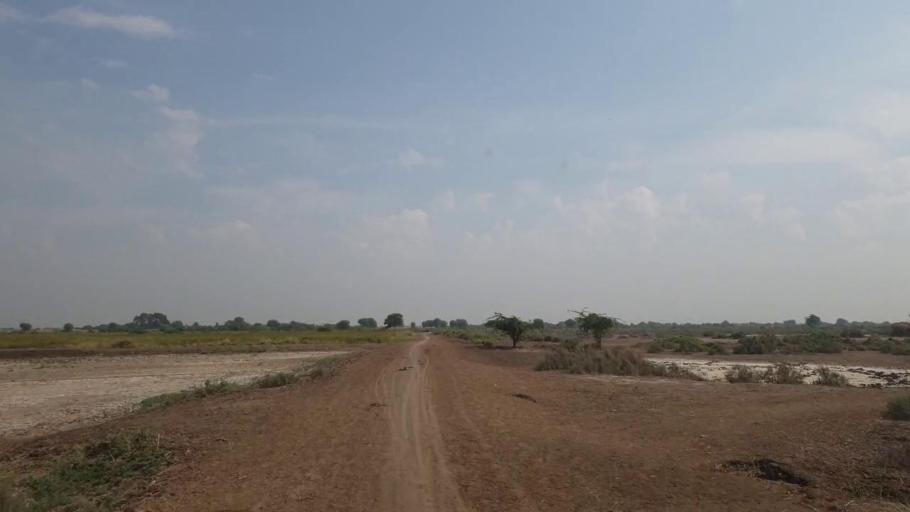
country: PK
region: Sindh
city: Rajo Khanani
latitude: 24.9542
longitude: 69.0244
